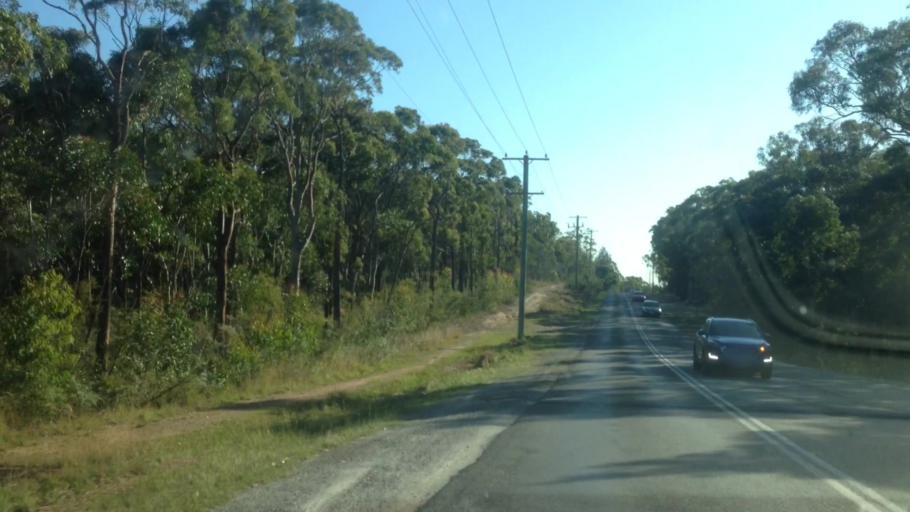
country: AU
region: New South Wales
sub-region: Lake Macquarie Shire
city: Dora Creek
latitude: -33.1069
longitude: 151.5442
